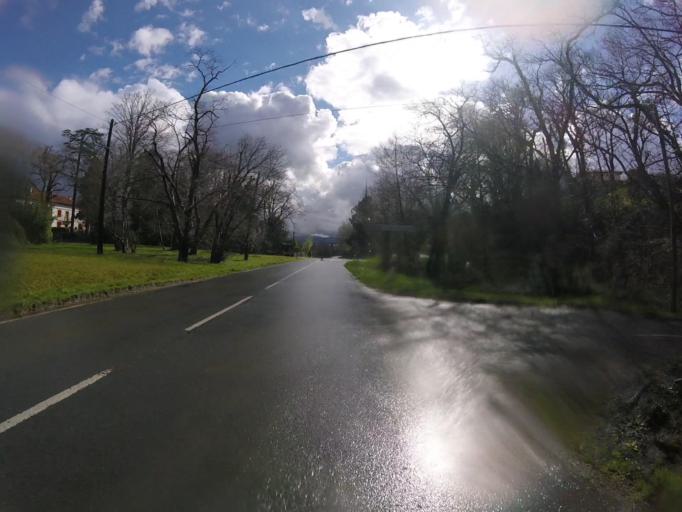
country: FR
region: Aquitaine
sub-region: Departement des Pyrenees-Atlantiques
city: Sare
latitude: 43.3148
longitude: -1.5791
